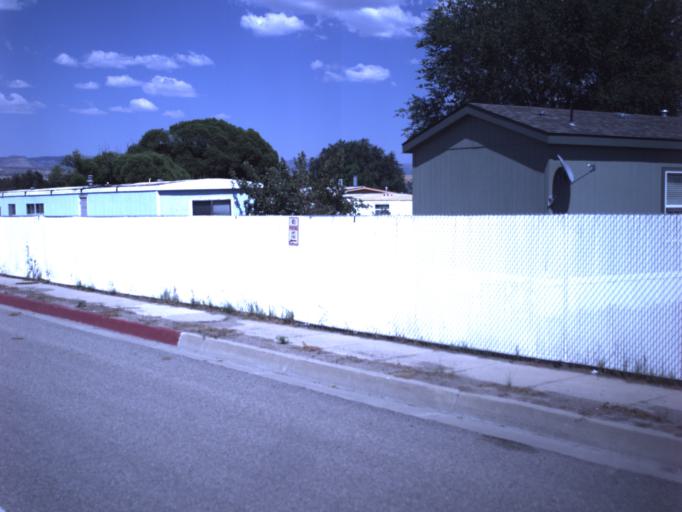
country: US
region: Utah
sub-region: Carbon County
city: Price
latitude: 39.5848
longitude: -110.8136
